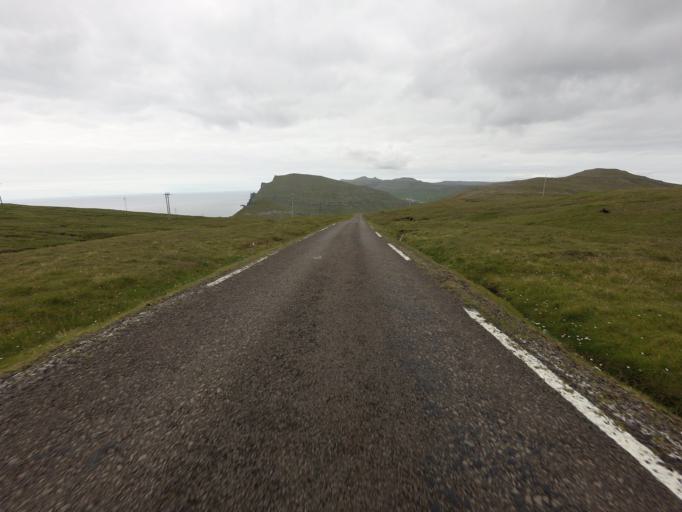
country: FO
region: Suduroy
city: Vagur
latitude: 61.4297
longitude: -6.7577
